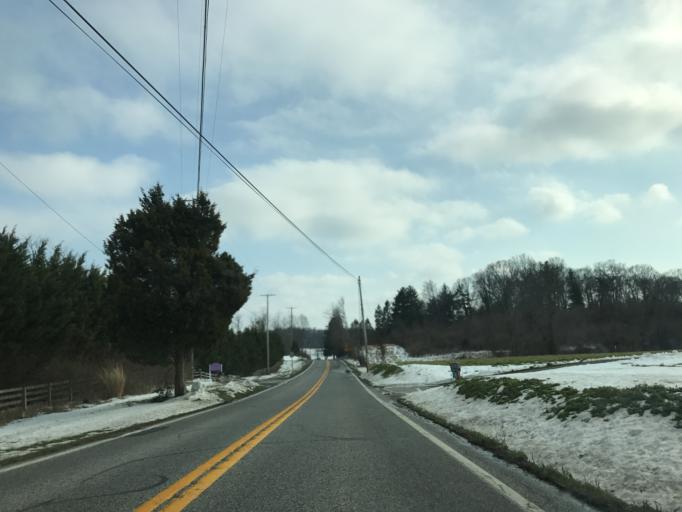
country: US
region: Maryland
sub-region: Harford County
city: South Bel Air
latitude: 39.5811
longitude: -76.2586
